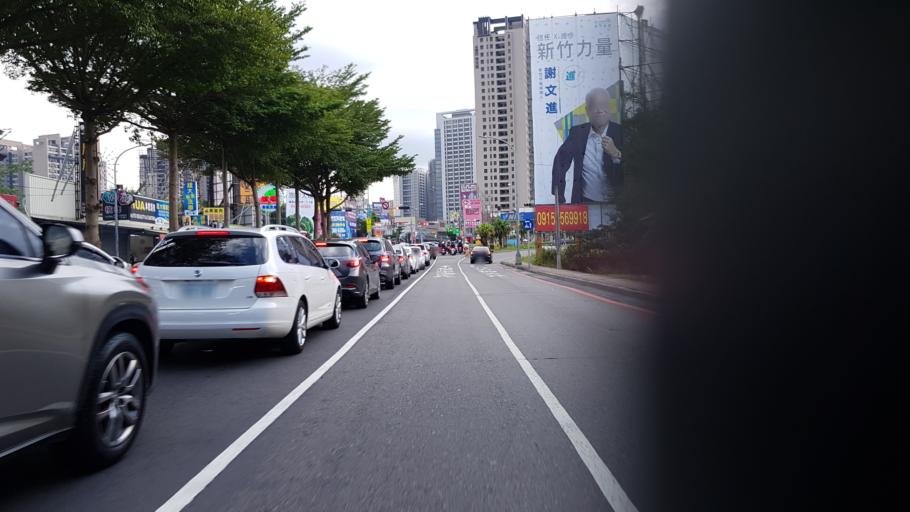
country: TW
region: Taiwan
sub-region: Hsinchu
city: Zhubei
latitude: 24.7969
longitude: 121.0133
